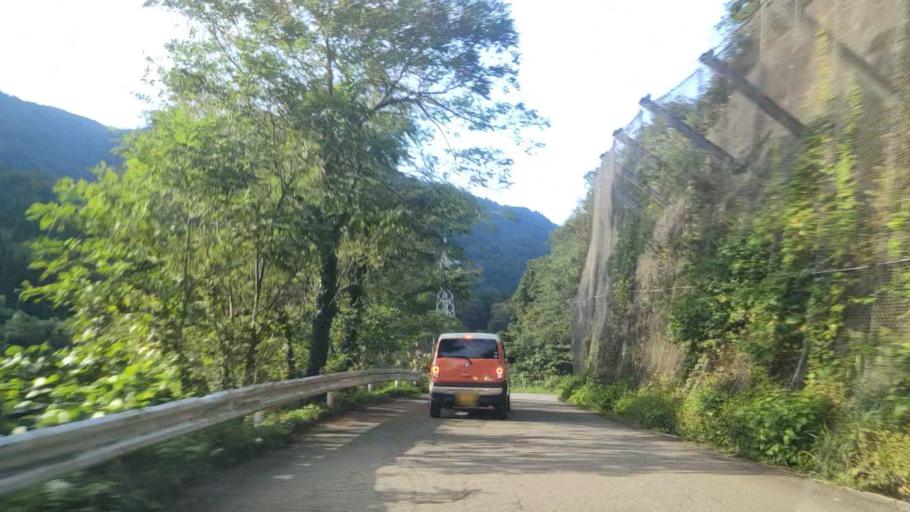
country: JP
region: Toyama
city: Yatsuomachi-higashikumisaka
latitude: 36.4522
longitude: 137.0849
